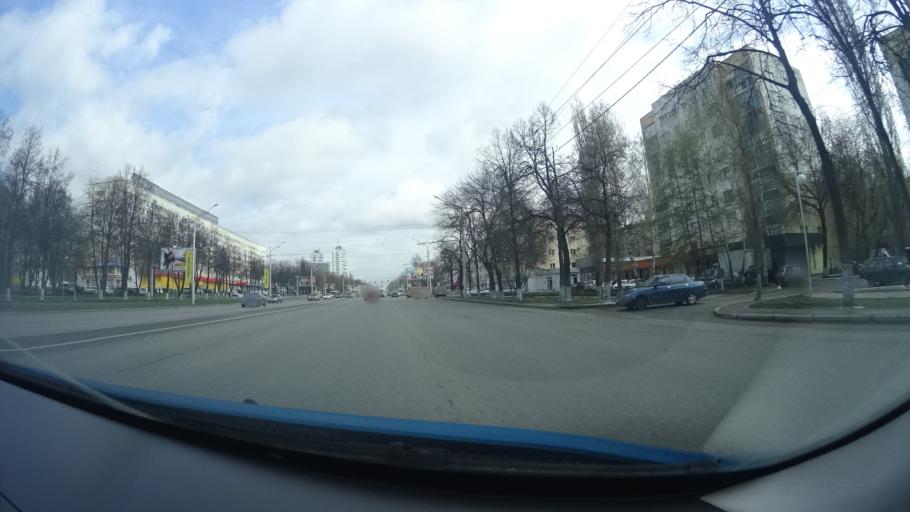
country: RU
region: Bashkortostan
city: Ufa
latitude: 54.7583
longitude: 56.0081
